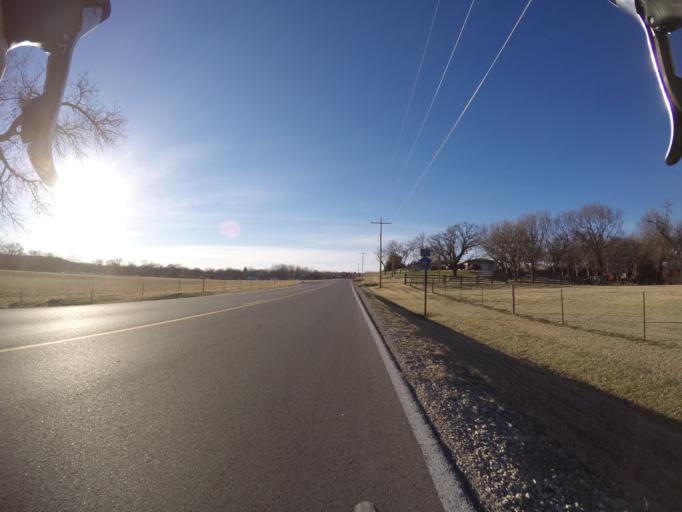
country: US
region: Kansas
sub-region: Riley County
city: Ogden
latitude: 39.2205
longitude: -96.7014
